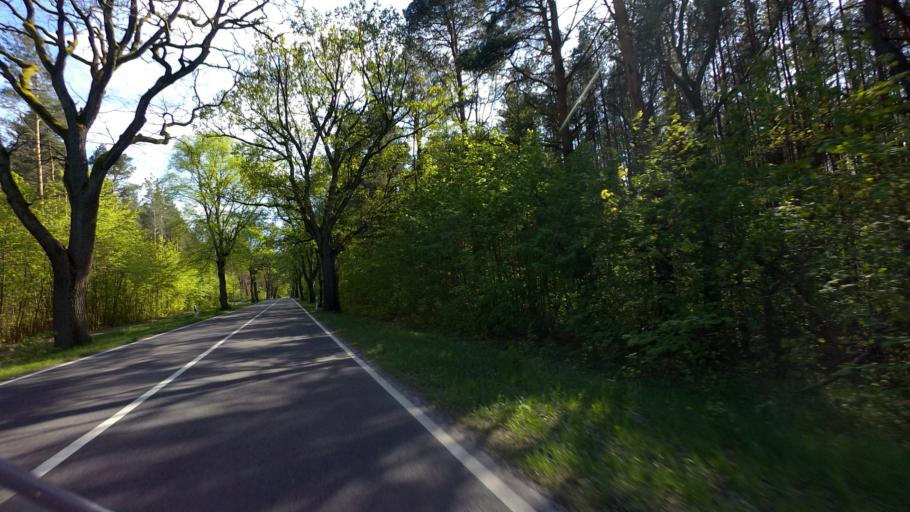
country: DE
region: Brandenburg
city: Milmersdorf
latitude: 53.0462
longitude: 13.6034
